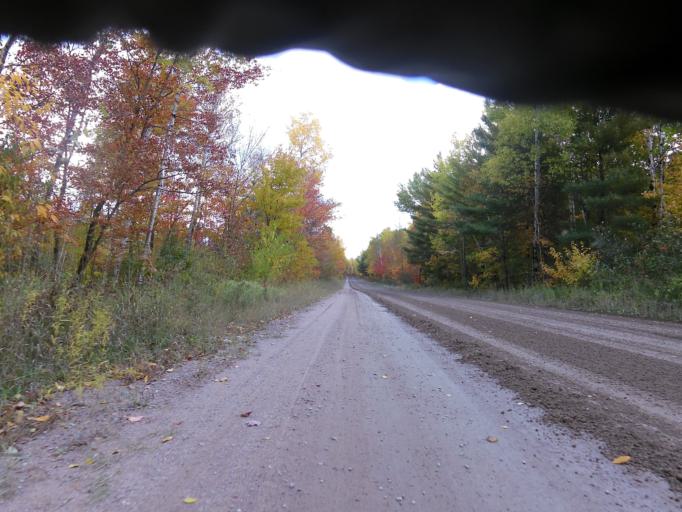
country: CA
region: Ontario
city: Petawawa
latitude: 45.8117
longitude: -77.3782
